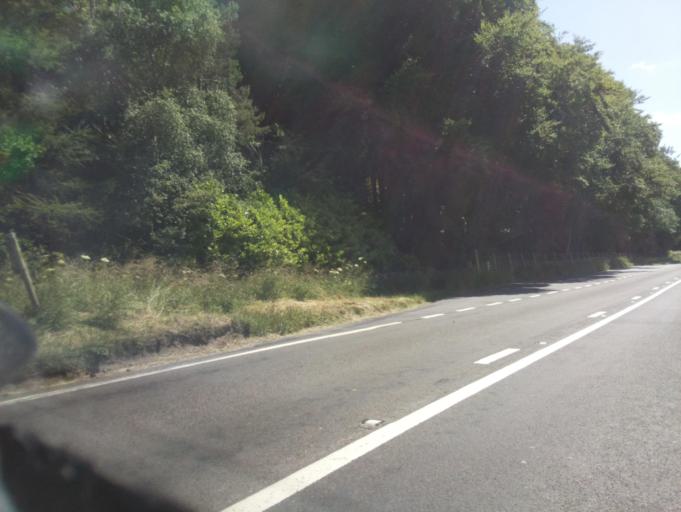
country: GB
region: England
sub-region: Derbyshire
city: Buxton
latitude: 53.2342
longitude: -1.8859
